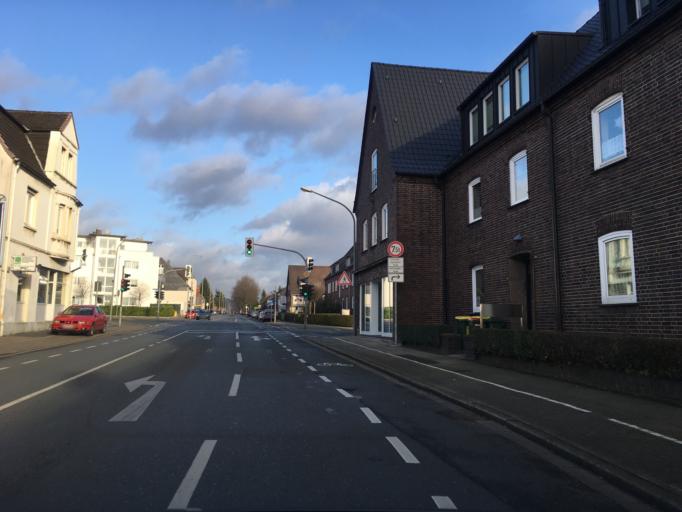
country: DE
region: North Rhine-Westphalia
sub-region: Regierungsbezirk Dusseldorf
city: Oberhausen
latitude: 51.5295
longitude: 6.8543
